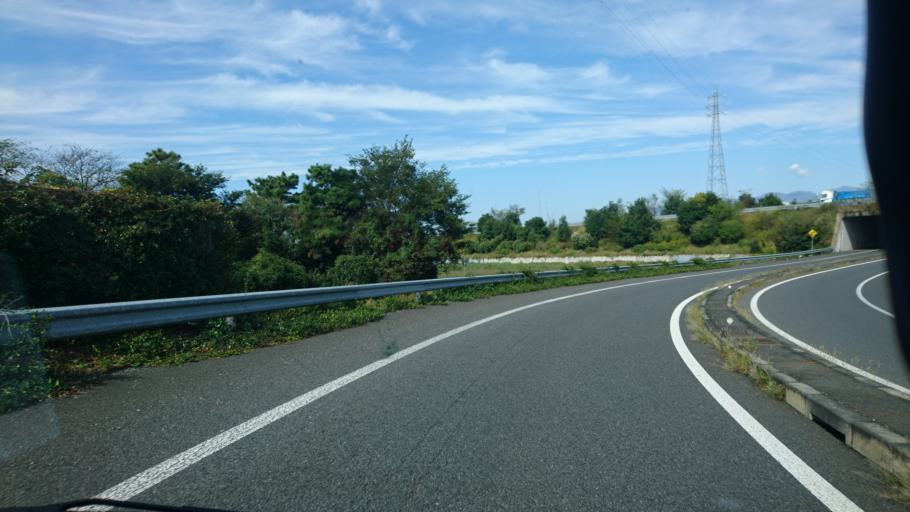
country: JP
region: Gunma
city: Kiryu
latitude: 36.3460
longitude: 139.2771
